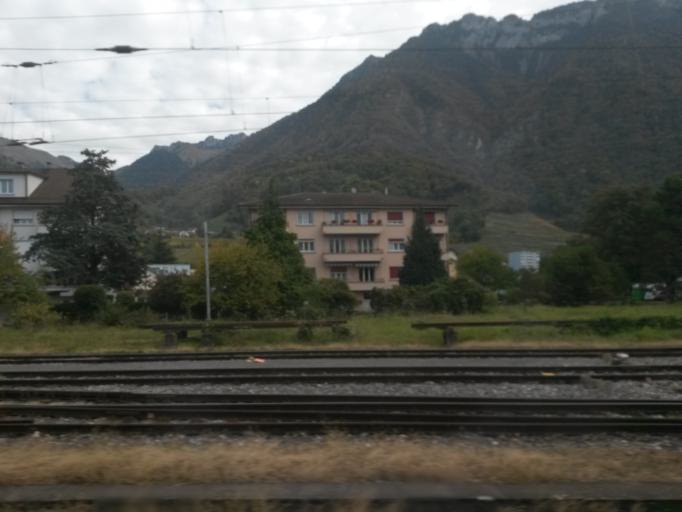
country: CH
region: Vaud
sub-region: Aigle District
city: Villeneuve
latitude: 46.3969
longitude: 6.9271
